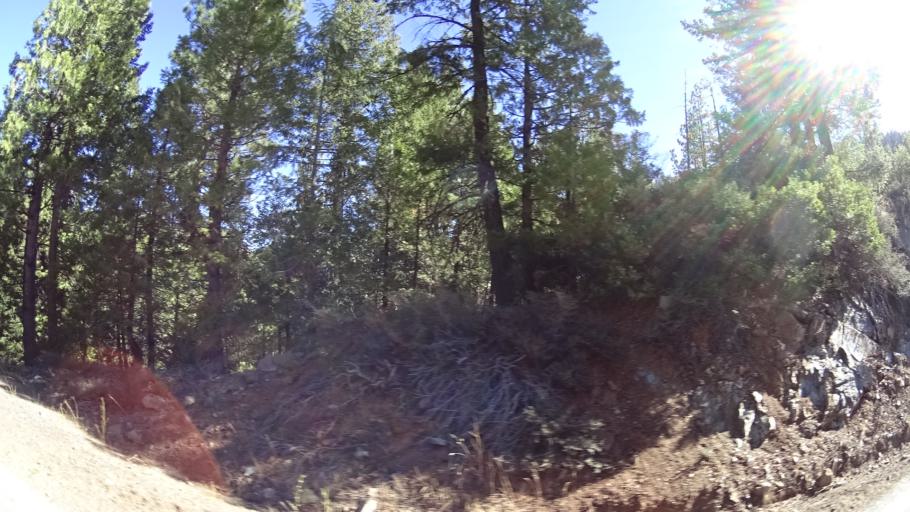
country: US
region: California
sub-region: Siskiyou County
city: Weed
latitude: 41.2650
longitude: -122.8832
